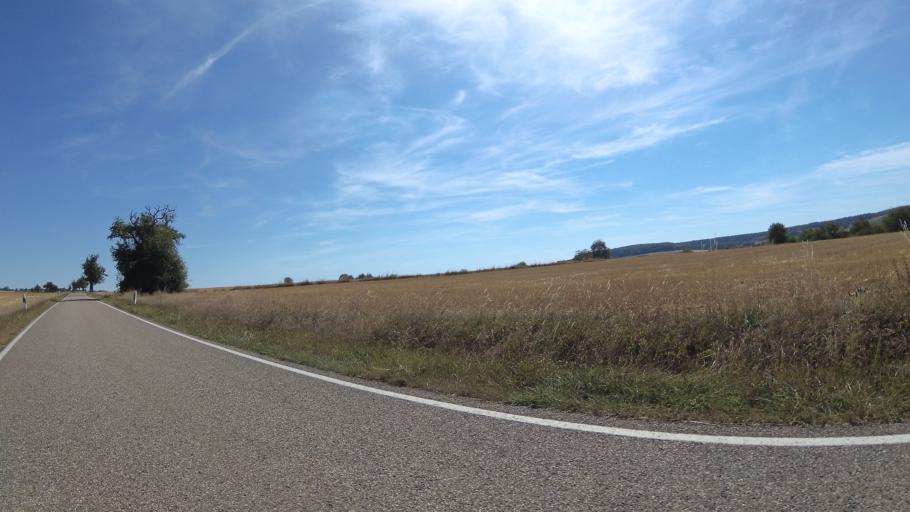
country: FR
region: Lorraine
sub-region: Departement de la Moselle
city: Petit-Rederching
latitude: 49.1387
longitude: 7.2907
